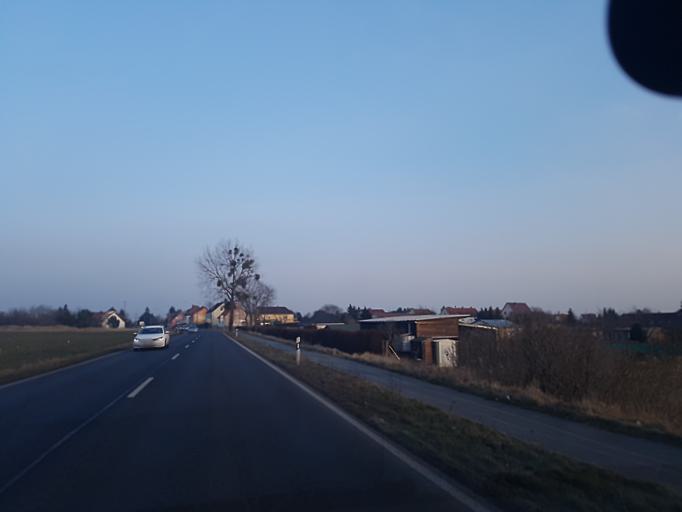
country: DE
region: Saxony-Anhalt
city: Nudersdorf
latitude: 51.8772
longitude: 12.5401
